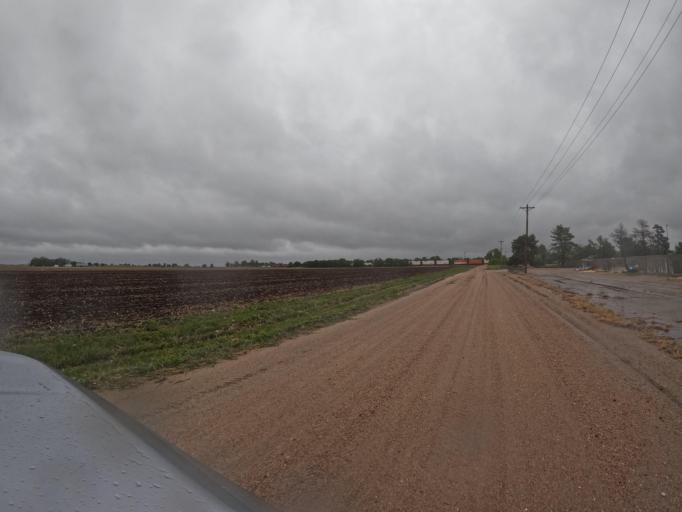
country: US
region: Nebraska
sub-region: Clay County
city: Harvard
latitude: 40.6133
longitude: -98.1027
